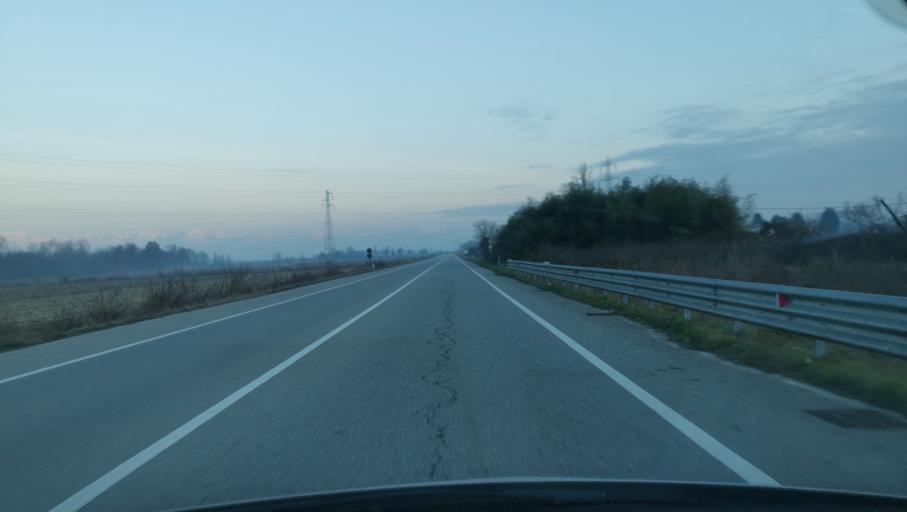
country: IT
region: Piedmont
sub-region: Provincia di Torino
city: Chivasso
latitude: 45.2212
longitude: 7.8906
